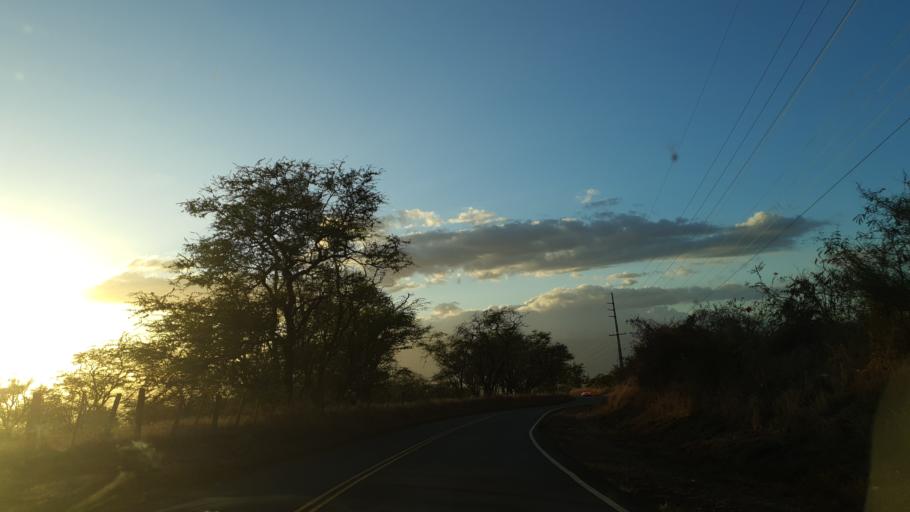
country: US
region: Hawaii
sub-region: Maui County
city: Pukalani
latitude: 20.7945
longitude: -156.3661
